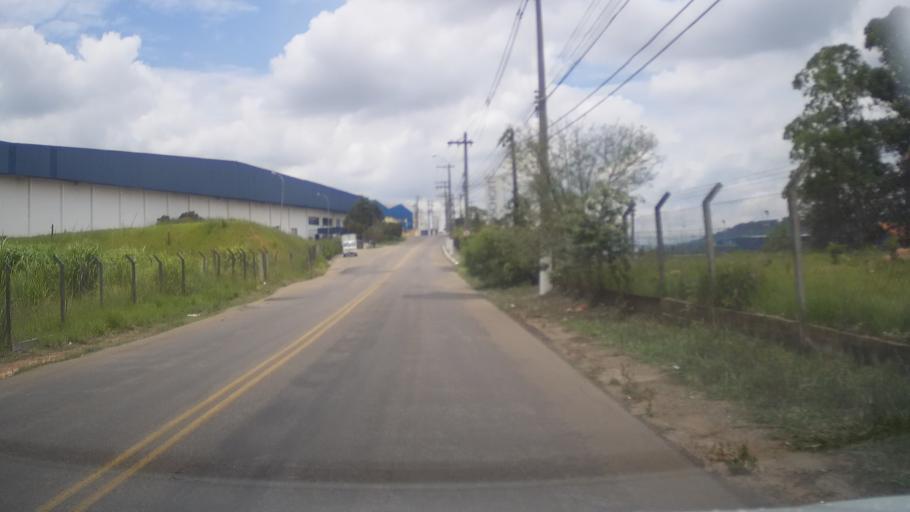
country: BR
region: Sao Paulo
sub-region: Itupeva
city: Itupeva
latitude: -23.1542
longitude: -47.0328
